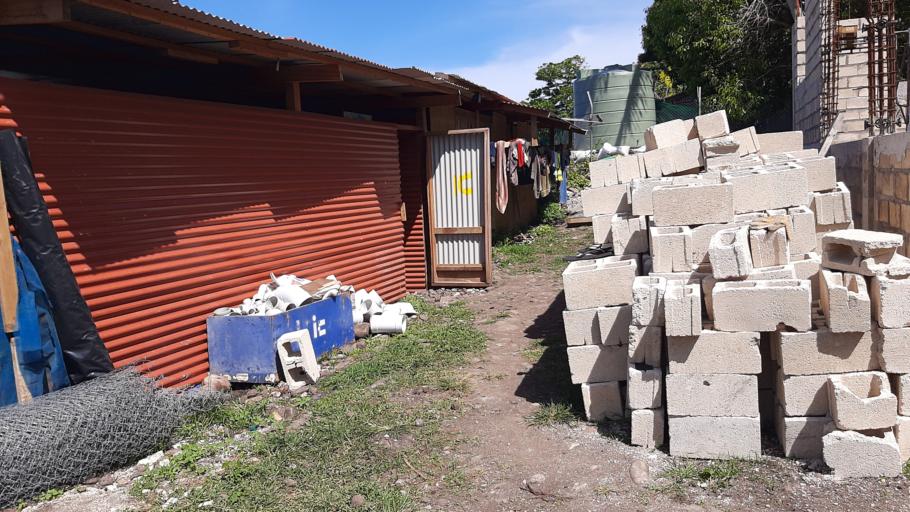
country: VU
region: Tafea
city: Isangel
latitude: -18.8176
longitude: 169.0157
